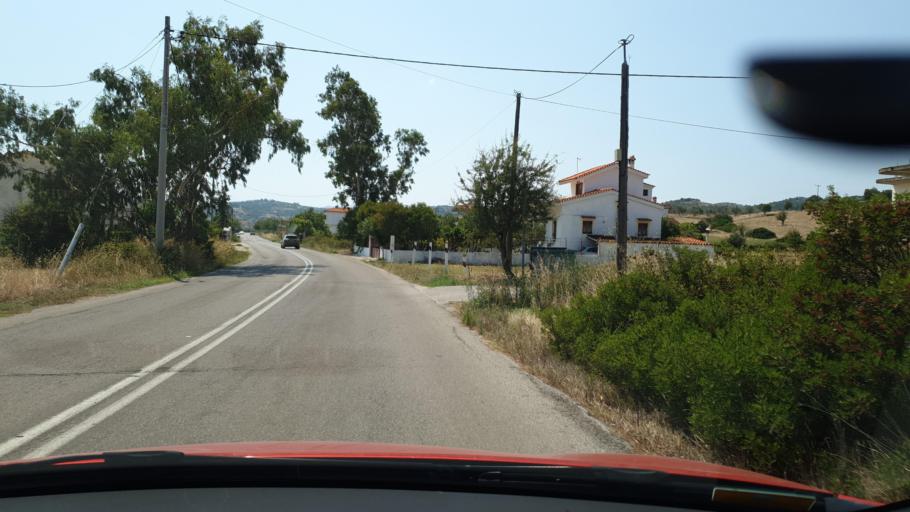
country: GR
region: Central Greece
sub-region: Nomos Evvoias
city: Aliveri
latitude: 38.4629
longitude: 24.1171
